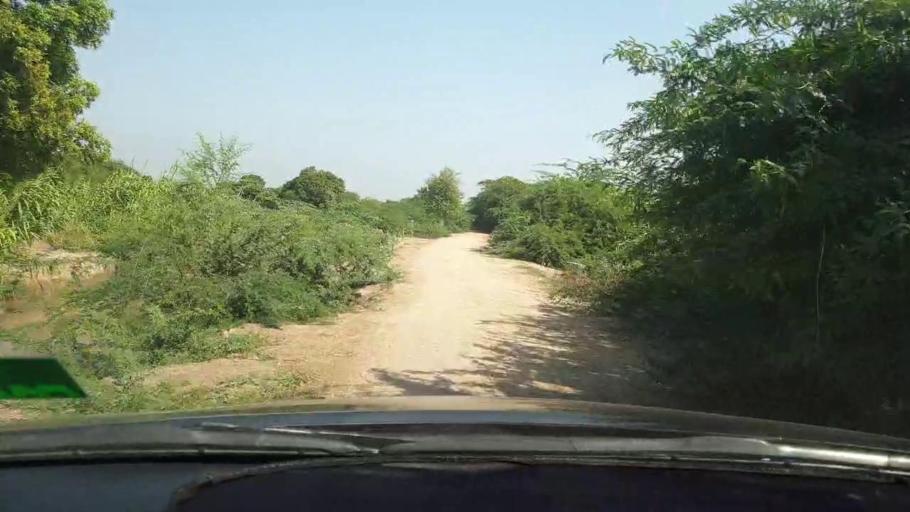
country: PK
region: Sindh
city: Tando Bago
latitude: 24.7751
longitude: 68.9458
